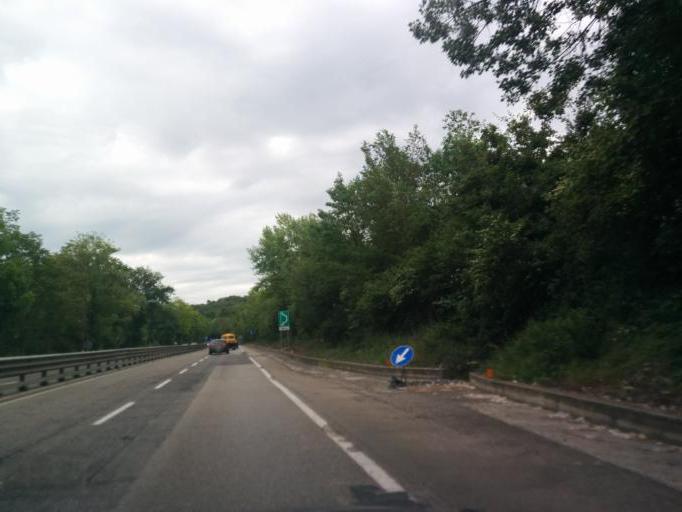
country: IT
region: Tuscany
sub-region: Provincia di Siena
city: Monteriggioni
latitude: 43.3936
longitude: 11.2324
